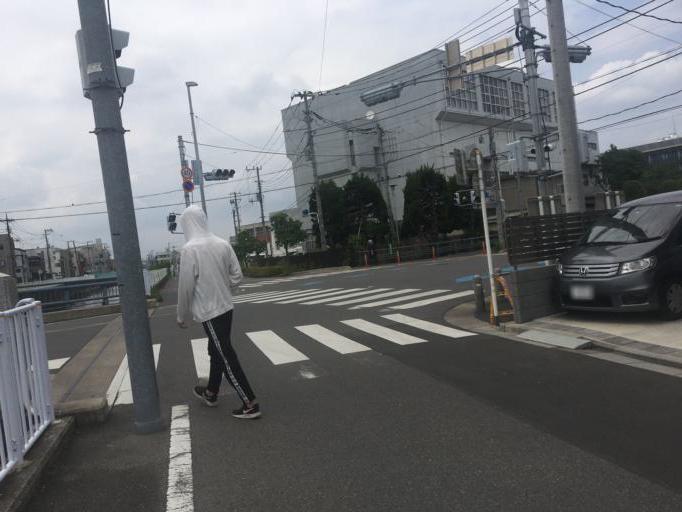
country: JP
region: Saitama
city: Kawaguchi
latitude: 35.8247
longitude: 139.7209
